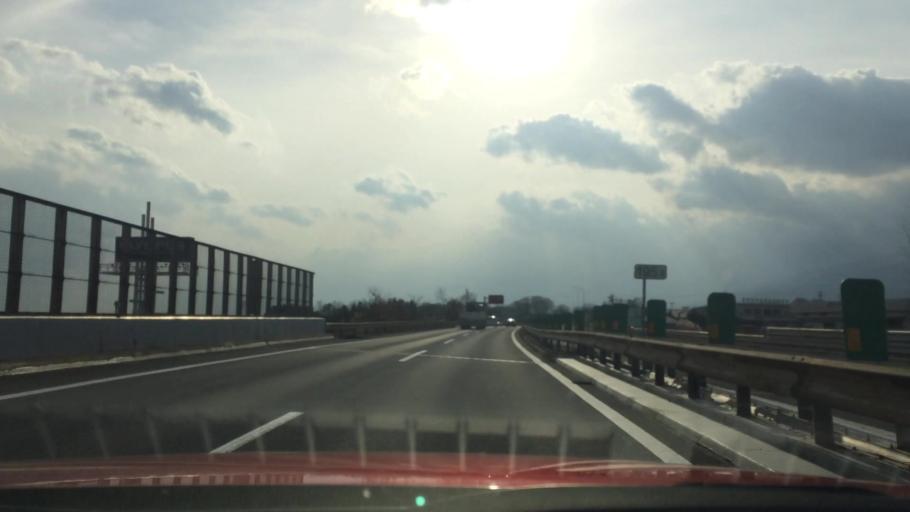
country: JP
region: Nagano
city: Tatsuno
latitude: 35.9479
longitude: 137.9864
